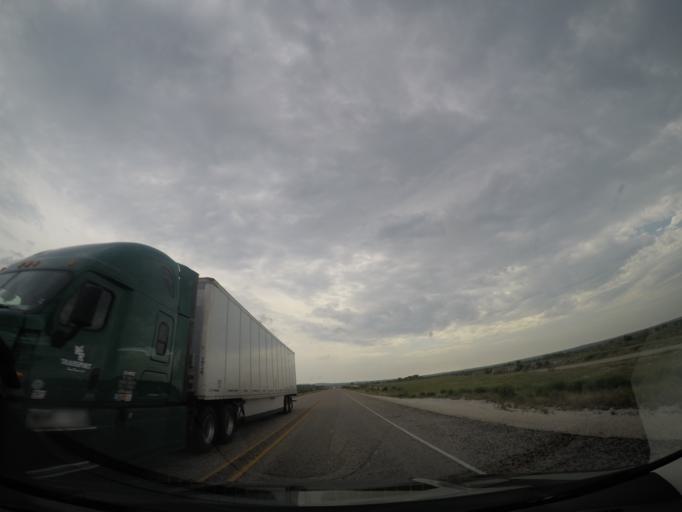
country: US
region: Texas
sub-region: Val Verde County
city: Cienegas Terrace
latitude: 29.7041
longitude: -101.3319
